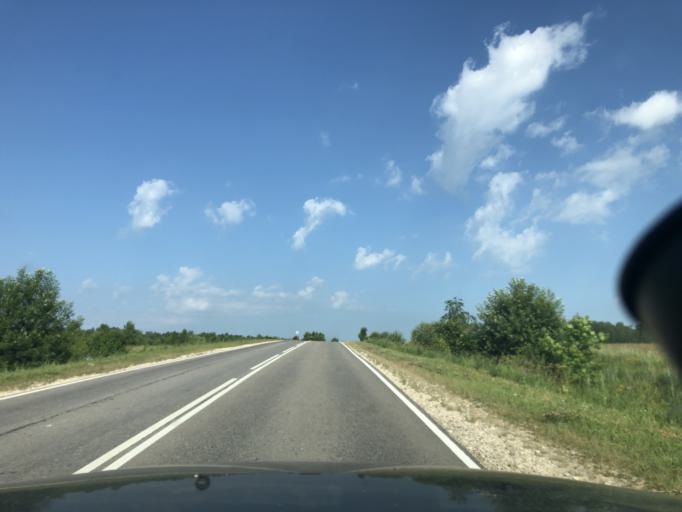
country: RU
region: Tula
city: Dubna
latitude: 54.1323
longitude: 37.0316
